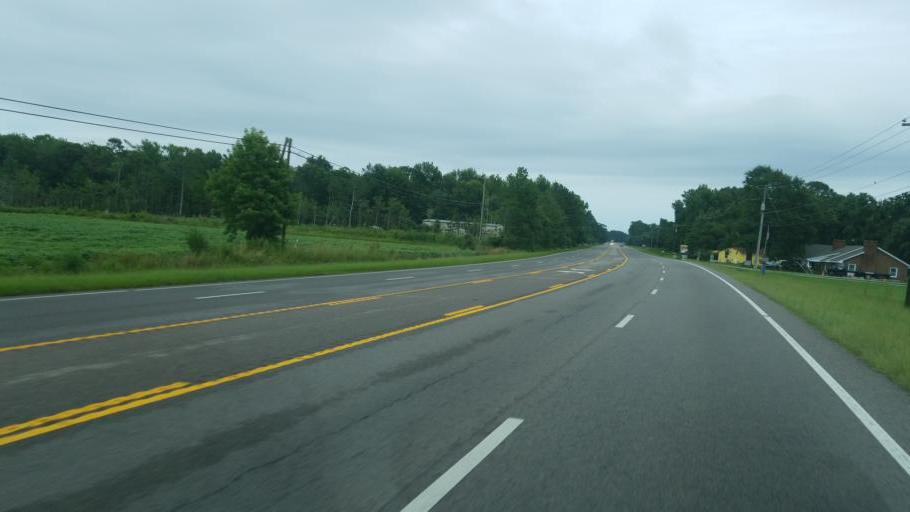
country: US
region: North Carolina
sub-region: Currituck County
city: Currituck
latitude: 36.2663
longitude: -75.9070
